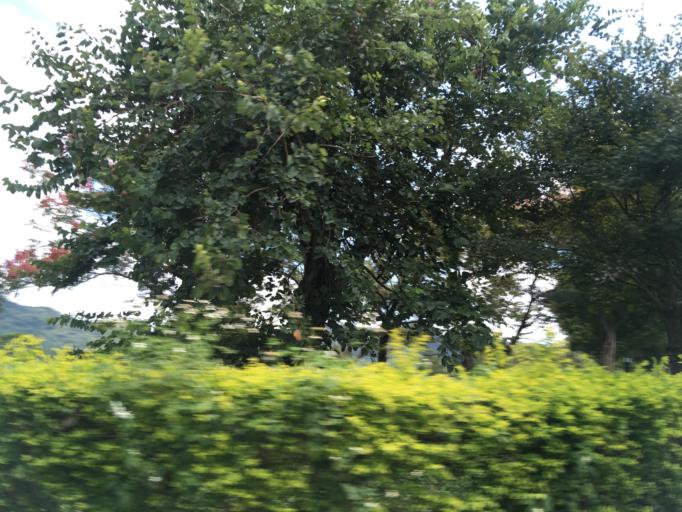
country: TW
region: Taipei
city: Taipei
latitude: 24.9353
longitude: 121.5796
